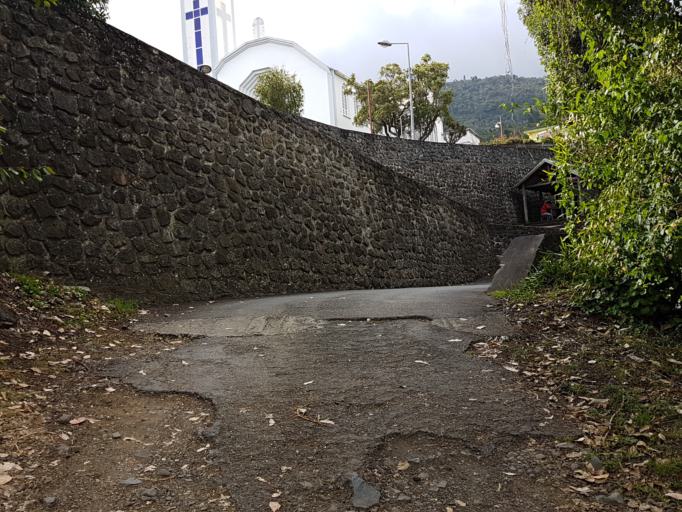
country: RE
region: Reunion
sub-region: Reunion
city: Cilaos
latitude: -21.1319
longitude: 55.4725
